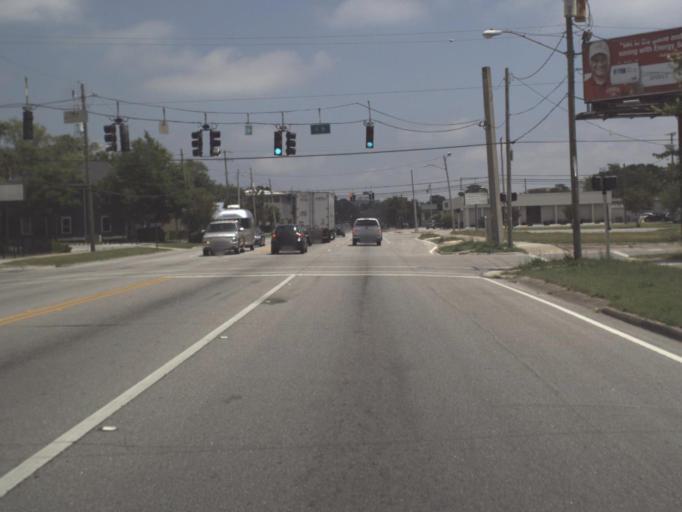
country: US
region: Florida
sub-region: Escambia County
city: Pensacola
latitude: 30.4114
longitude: -87.2310
